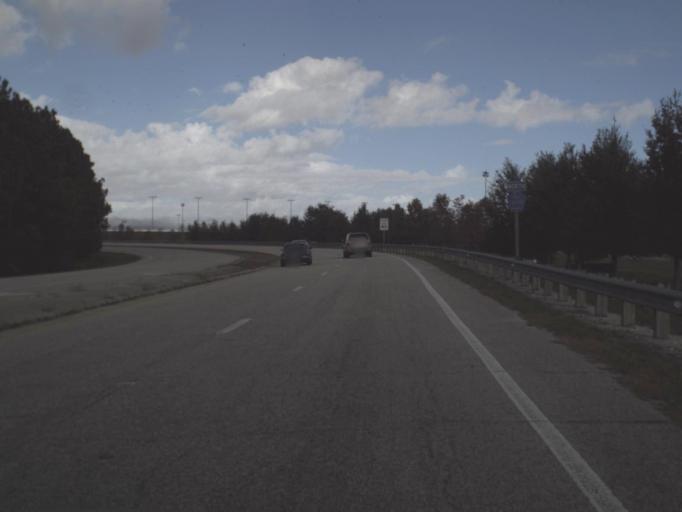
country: US
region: Florida
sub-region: Volusia County
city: Daytona Beach
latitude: 29.1753
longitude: -81.0781
